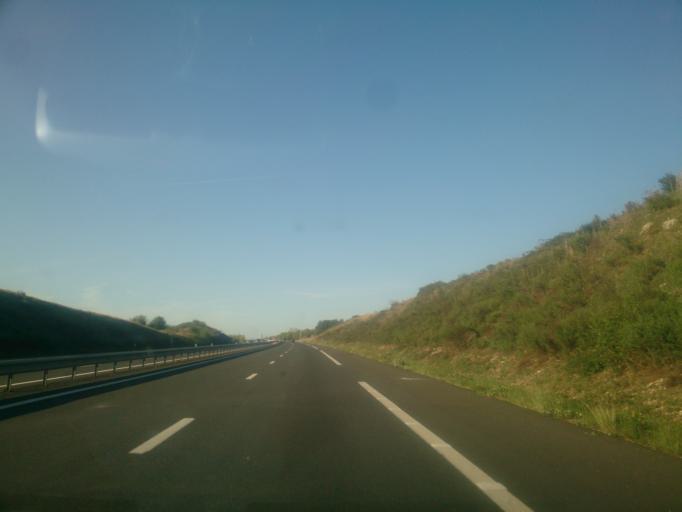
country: FR
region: Midi-Pyrenees
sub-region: Departement du Lot
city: Cahors
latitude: 44.5235
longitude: 1.5105
